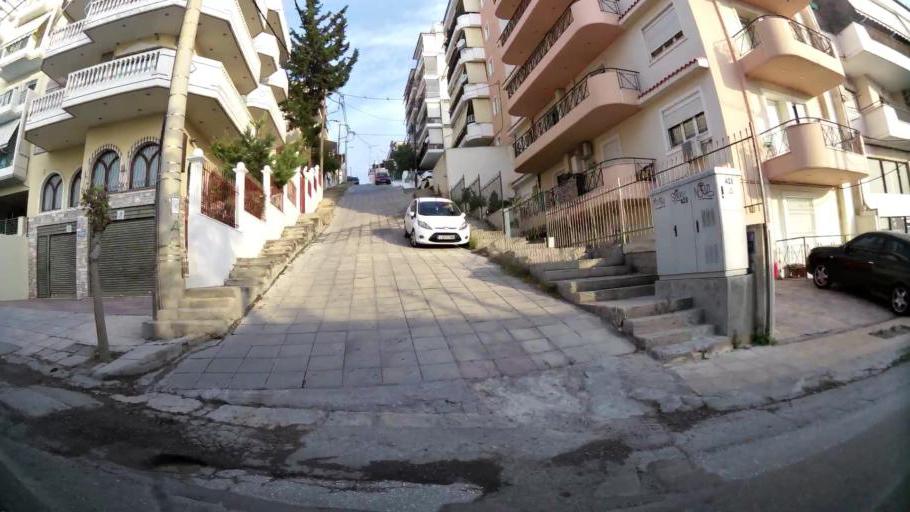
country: GR
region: Attica
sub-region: Nomarchia Dytikis Attikis
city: Zefyri
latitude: 38.0624
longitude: 23.7117
